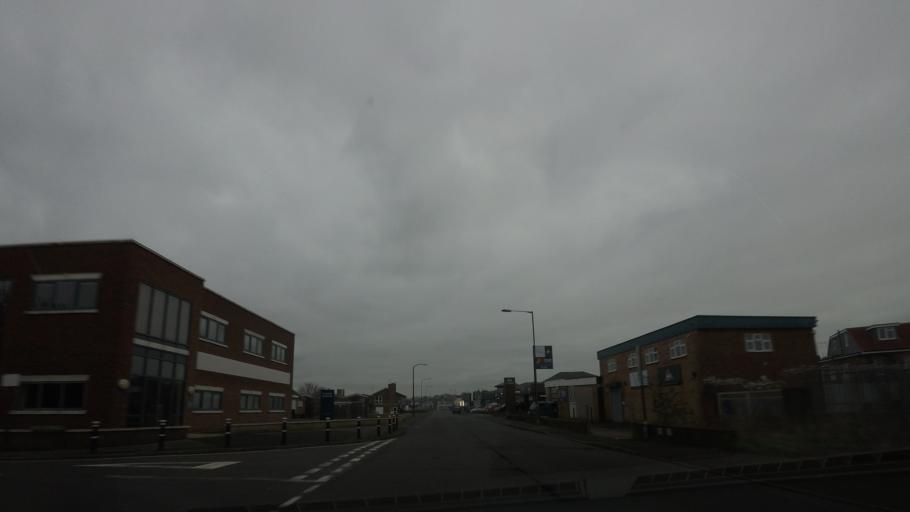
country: GB
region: England
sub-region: East Sussex
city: Bexhill-on-Sea
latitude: 50.8433
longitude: 0.4656
